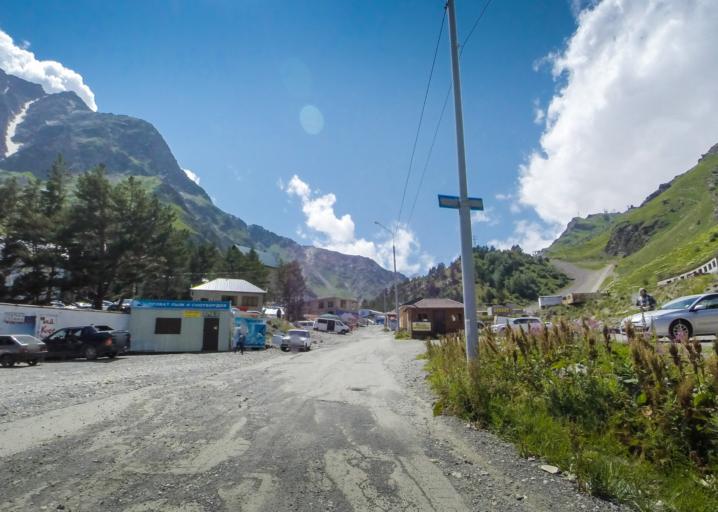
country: RU
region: Kabardino-Balkariya
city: Terskol
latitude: 43.2664
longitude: 42.4805
